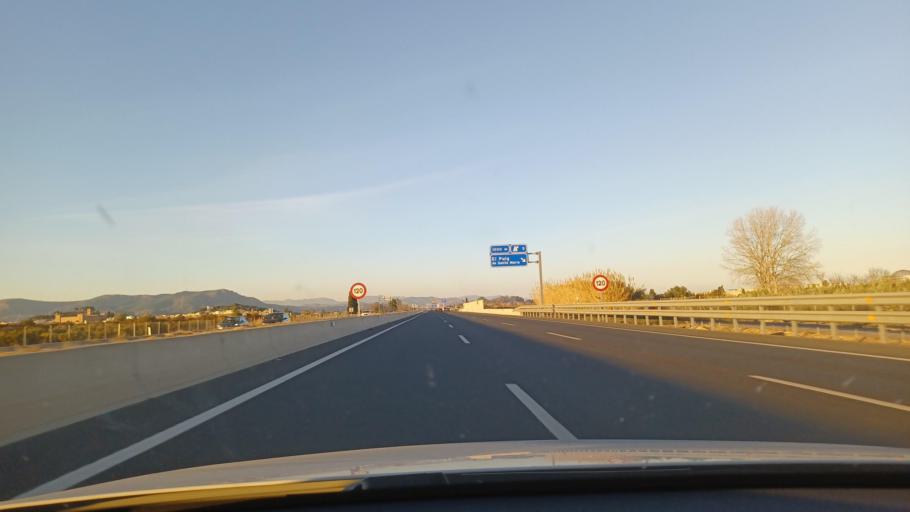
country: ES
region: Valencia
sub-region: Provincia de Valencia
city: Puig
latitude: 39.5729
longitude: -0.2953
